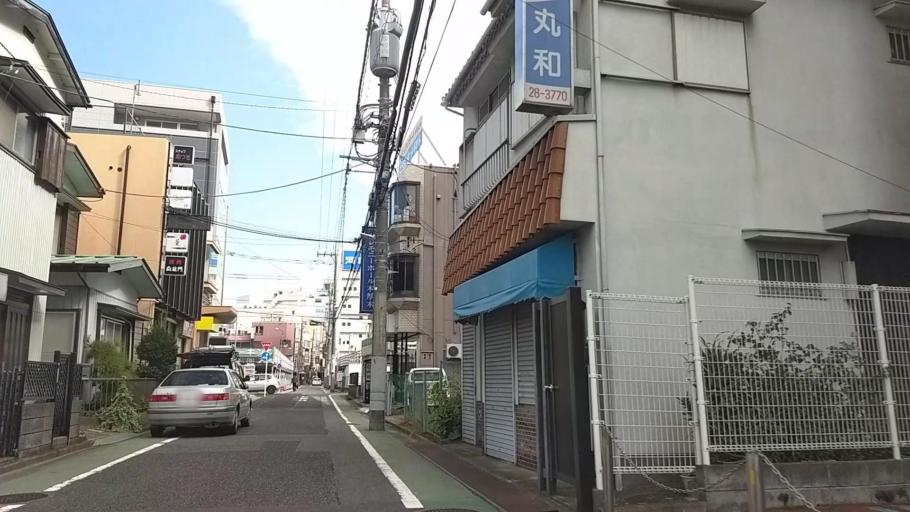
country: JP
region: Kanagawa
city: Atsugi
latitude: 35.4373
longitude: 139.3630
